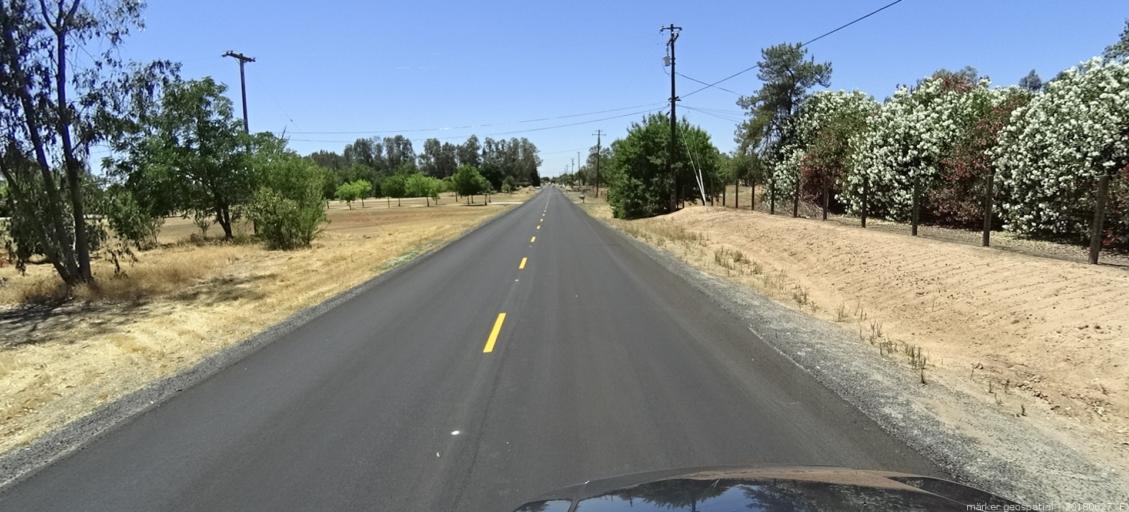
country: US
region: California
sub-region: Madera County
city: Bonadelle Ranchos-Madera Ranchos
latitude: 36.9330
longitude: -119.8972
